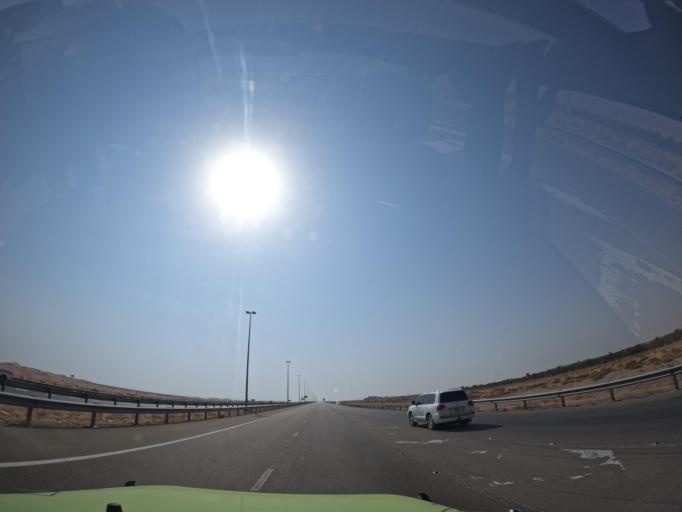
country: OM
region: Al Buraimi
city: Al Buraymi
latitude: 24.4064
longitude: 55.7069
